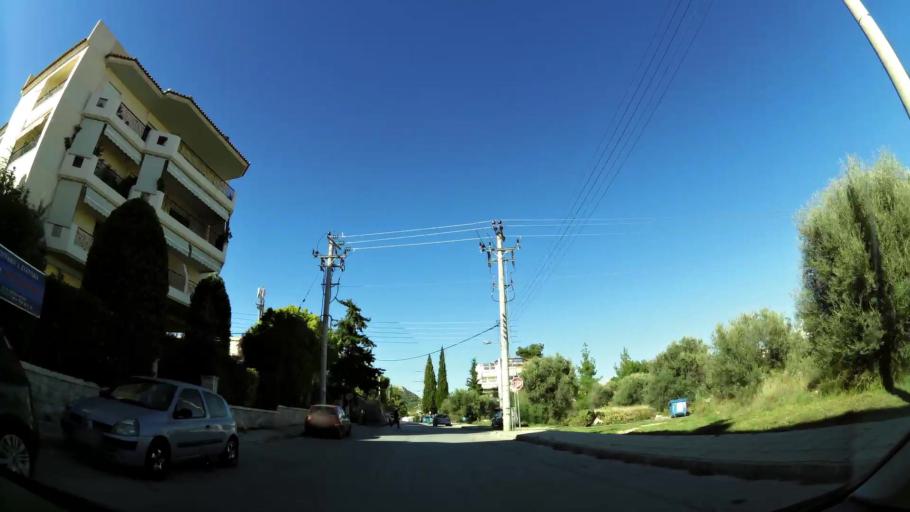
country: GR
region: Attica
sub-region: Nomarchia Anatolikis Attikis
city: Leondarion
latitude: 37.9887
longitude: 23.8488
